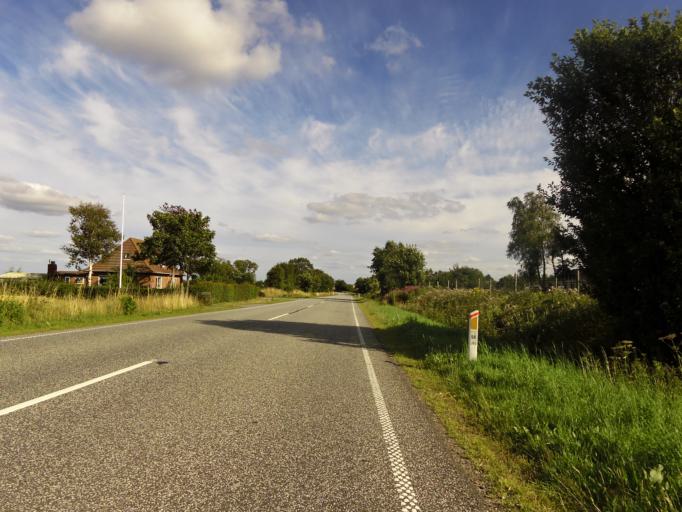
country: DK
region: South Denmark
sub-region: Tonder Kommune
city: Toftlund
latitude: 55.2250
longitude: 9.0028
